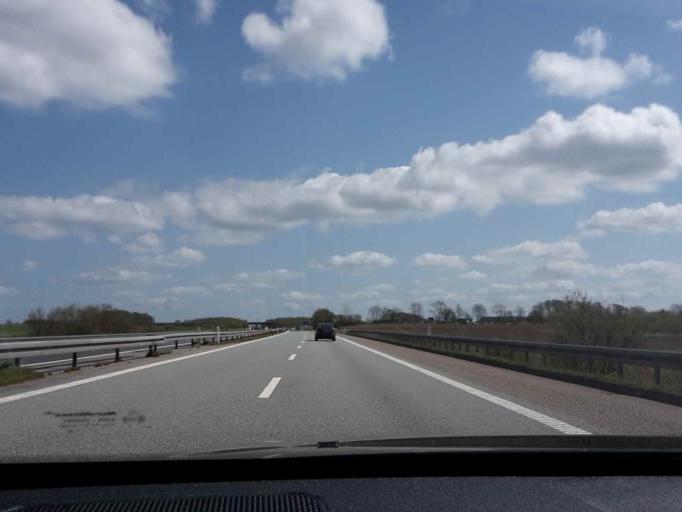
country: DK
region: South Denmark
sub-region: Vejen Kommune
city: Brorup
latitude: 55.5063
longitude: 9.0066
